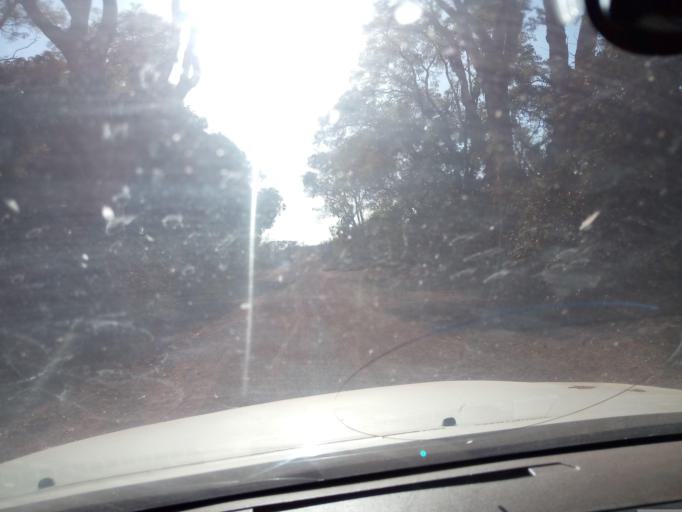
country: ML
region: Sikasso
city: Sikasso
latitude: 11.4800
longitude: -5.4947
